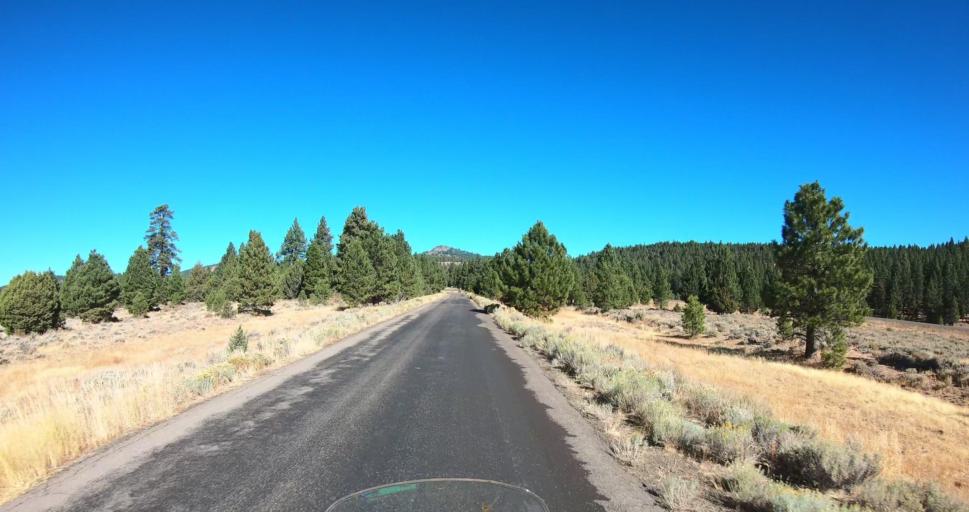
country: US
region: Oregon
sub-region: Lake County
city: Lakeview
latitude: 42.2224
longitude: -120.2292
